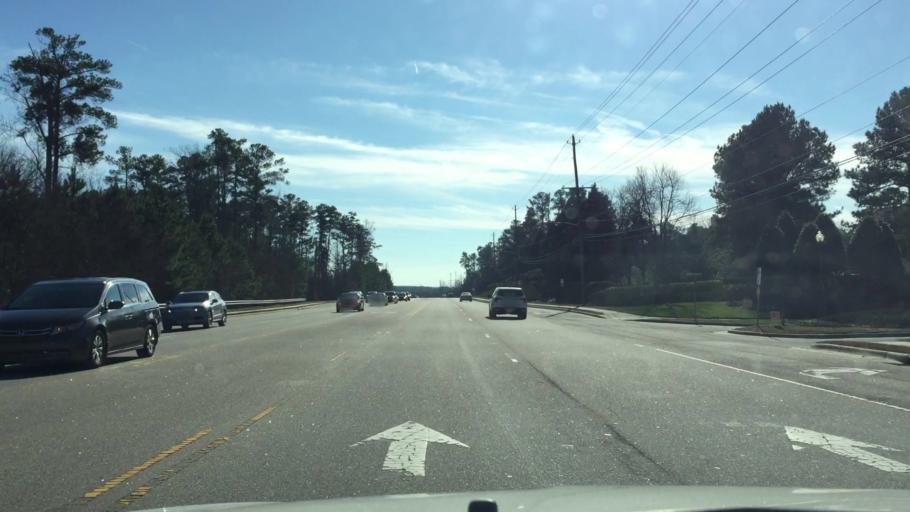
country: US
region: North Carolina
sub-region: Wake County
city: Apex
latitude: 35.7574
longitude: -78.8764
